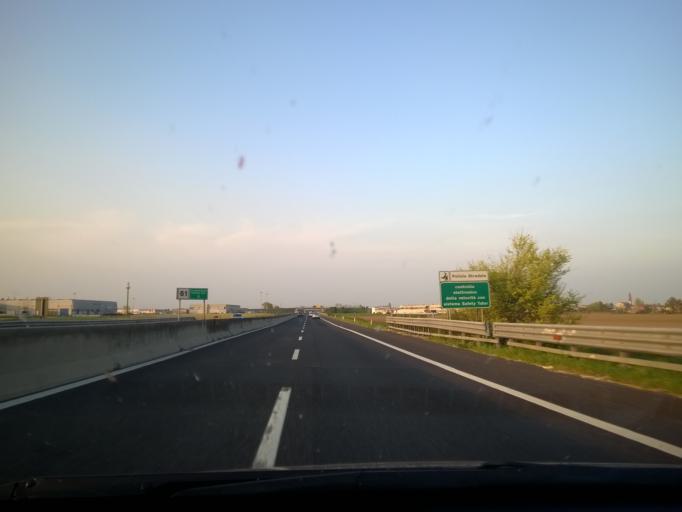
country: IT
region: Veneto
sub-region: Provincia di Rovigo
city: Villamarzana
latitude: 45.0104
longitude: 11.6832
